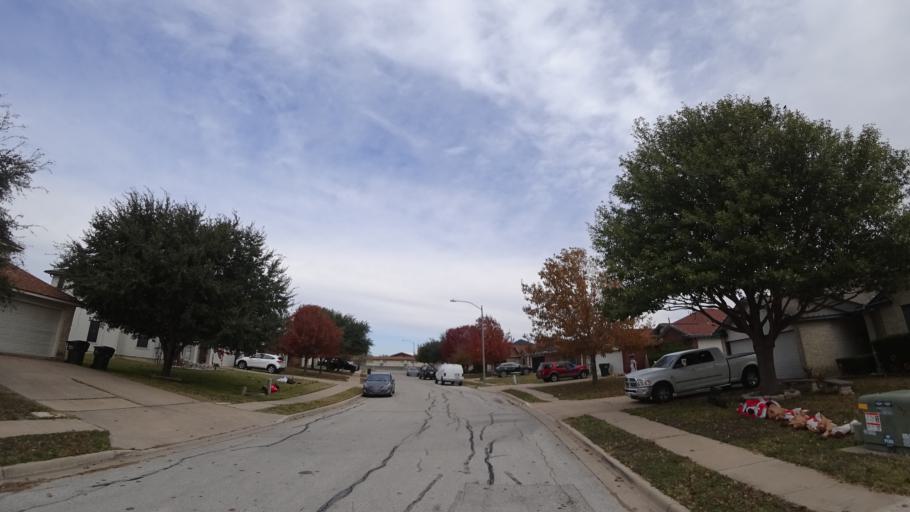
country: US
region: Texas
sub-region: Travis County
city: Garfield
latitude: 30.1553
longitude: -97.6446
